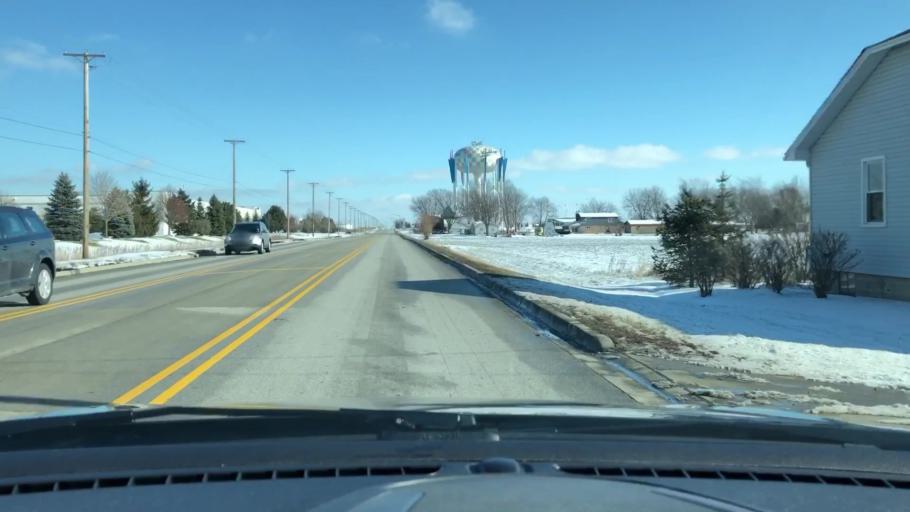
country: US
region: Illinois
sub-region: Will County
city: Preston Heights
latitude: 41.4809
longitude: -88.0747
